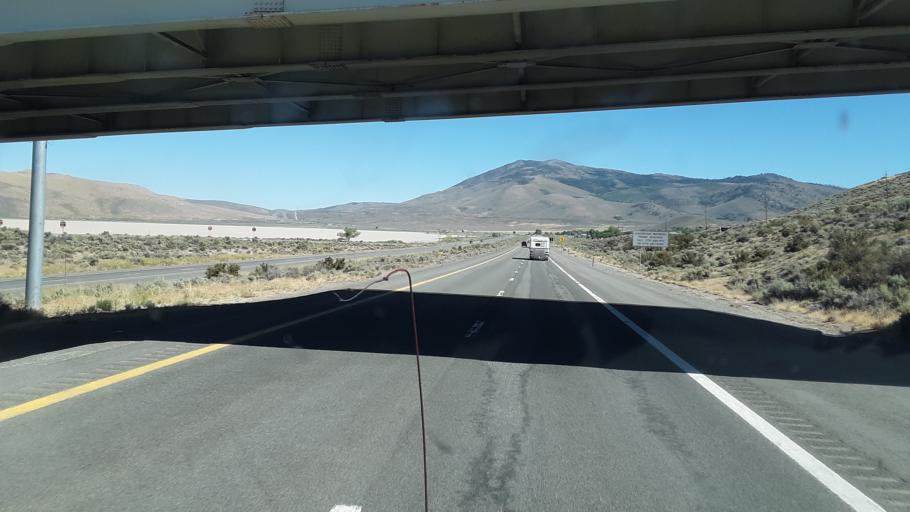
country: US
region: Nevada
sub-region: Washoe County
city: Cold Springs
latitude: 39.6683
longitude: -119.9969
